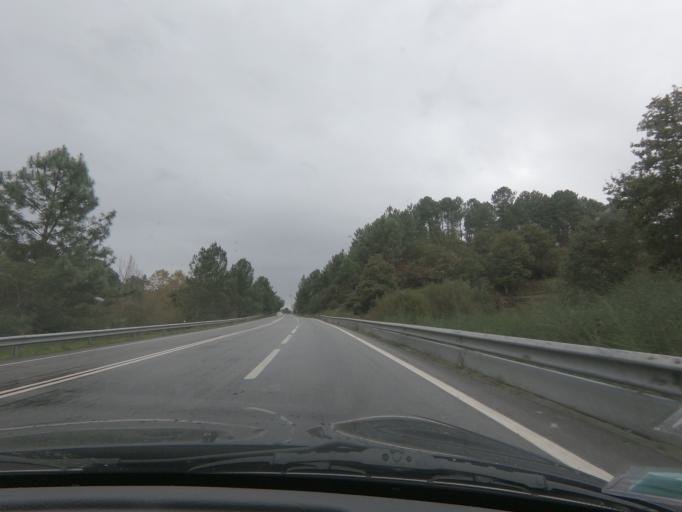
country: PT
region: Porto
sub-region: Amarante
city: Teloes
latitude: 41.3100
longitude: -8.0752
